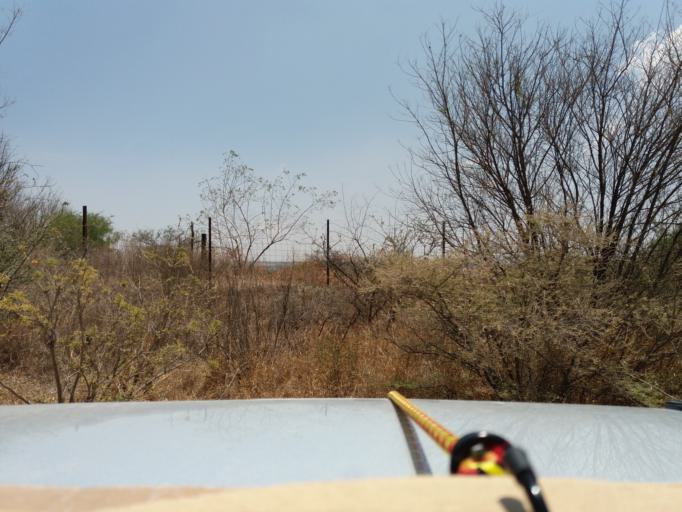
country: MX
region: Aguascalientes
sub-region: Aguascalientes
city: Penuelas (El Cienegal)
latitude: 21.7741
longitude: -102.3286
